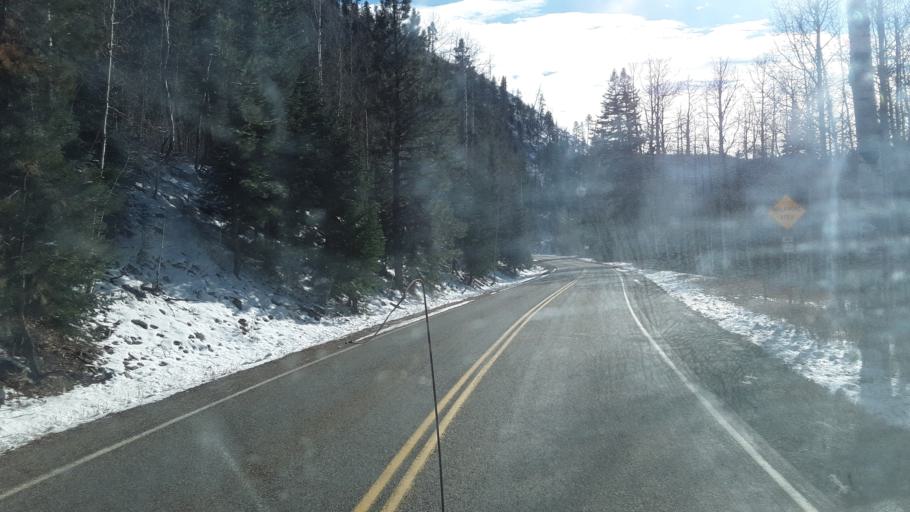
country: US
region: Colorado
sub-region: La Plata County
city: Bayfield
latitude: 37.3764
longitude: -107.6595
